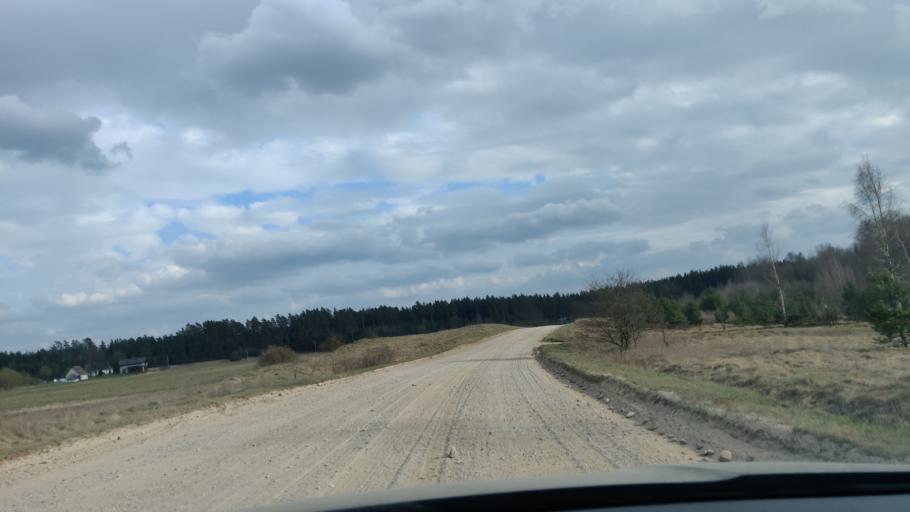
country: LT
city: Lentvaris
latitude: 54.6069
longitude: 25.0745
